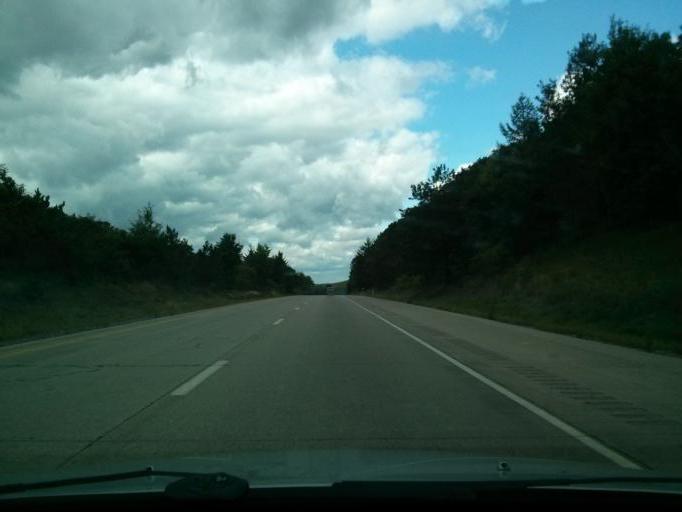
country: US
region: Pennsylvania
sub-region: Jefferson County
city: Reynoldsville
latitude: 41.1526
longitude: -78.9155
